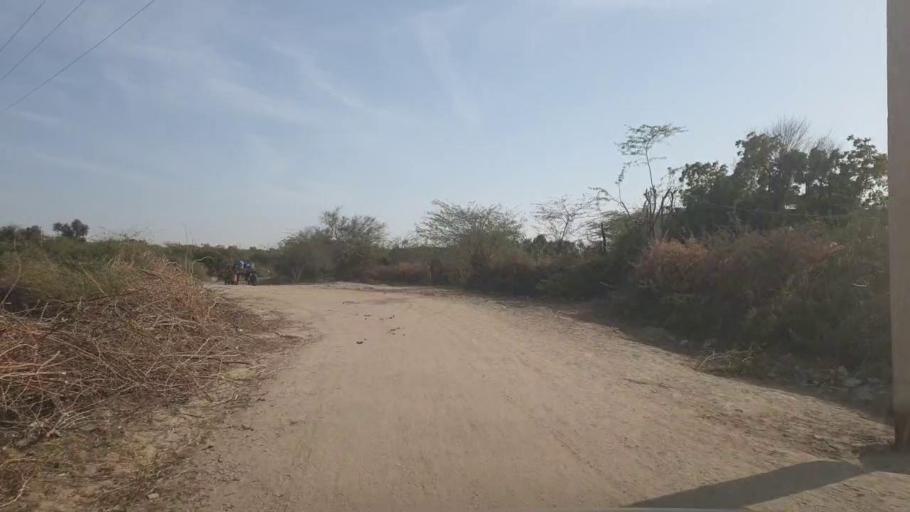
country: PK
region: Sindh
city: Nabisar
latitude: 25.0660
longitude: 69.6396
